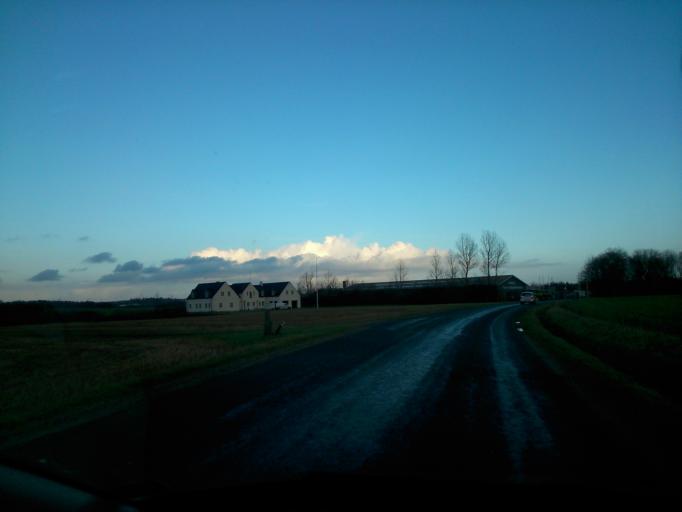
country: DK
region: Central Jutland
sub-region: Ringkobing-Skjern Kommune
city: Videbaek
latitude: 56.0650
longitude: 8.5870
